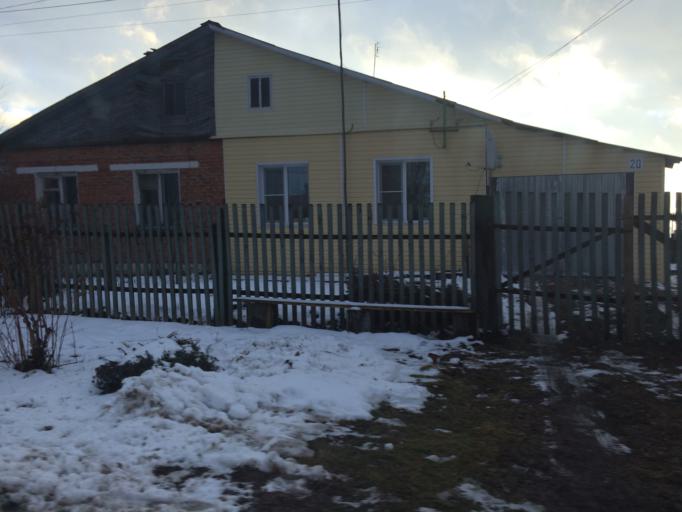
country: RU
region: Tula
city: Cherepet'
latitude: 54.1073
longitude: 36.3299
